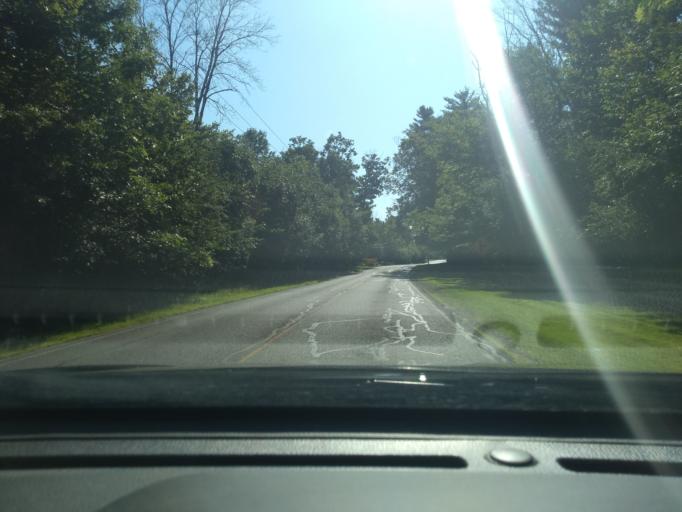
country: US
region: New York
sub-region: Erie County
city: Billington Heights
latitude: 42.7782
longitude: -78.6593
